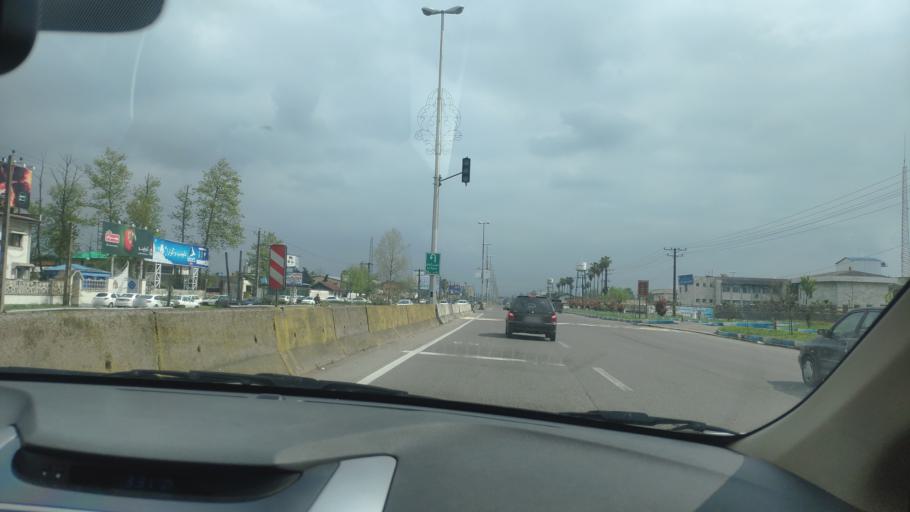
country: IR
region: Gilan
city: Rasht
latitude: 37.2354
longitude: 49.6267
